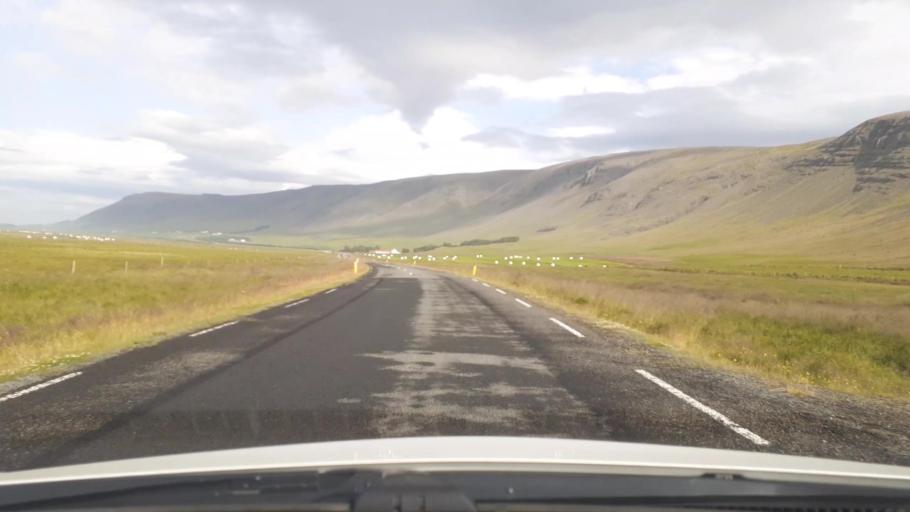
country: IS
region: Capital Region
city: Mosfellsbaer
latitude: 64.3277
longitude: -21.5065
